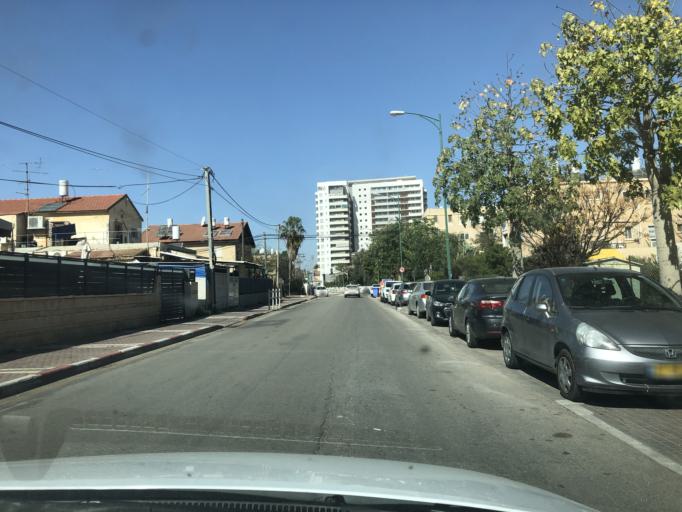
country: IL
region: Southern District
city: Beersheba
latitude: 31.2569
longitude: 34.7952
